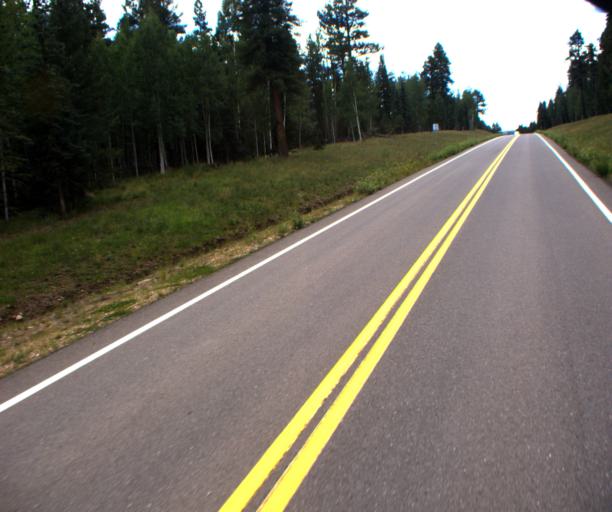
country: US
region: Arizona
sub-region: Apache County
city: Eagar
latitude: 33.9790
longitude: -109.5014
